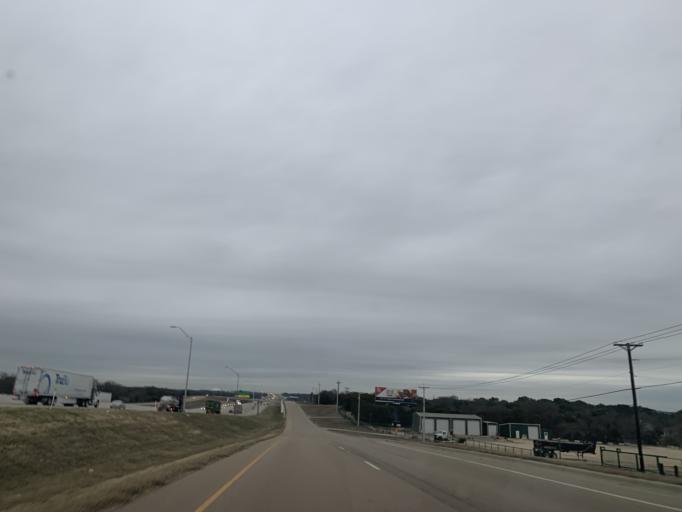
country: US
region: Texas
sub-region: Bell County
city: Salado
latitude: 30.9910
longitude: -97.4988
